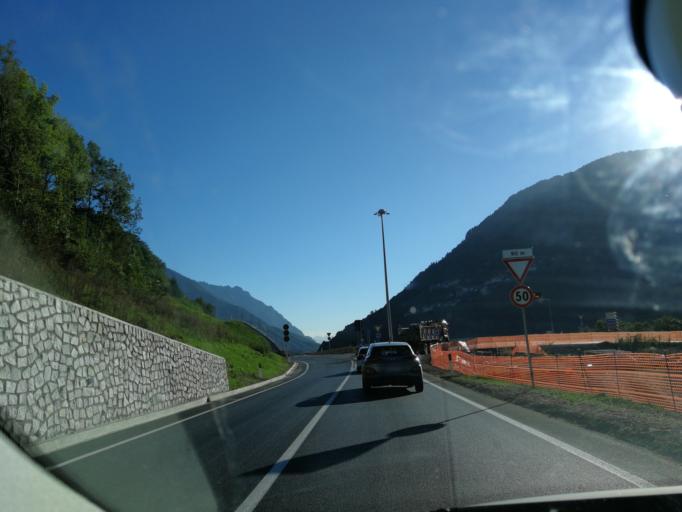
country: IT
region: Trentino-Alto Adige
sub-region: Provincia di Trento
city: Pieve di Bono
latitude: 45.9437
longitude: 10.6450
